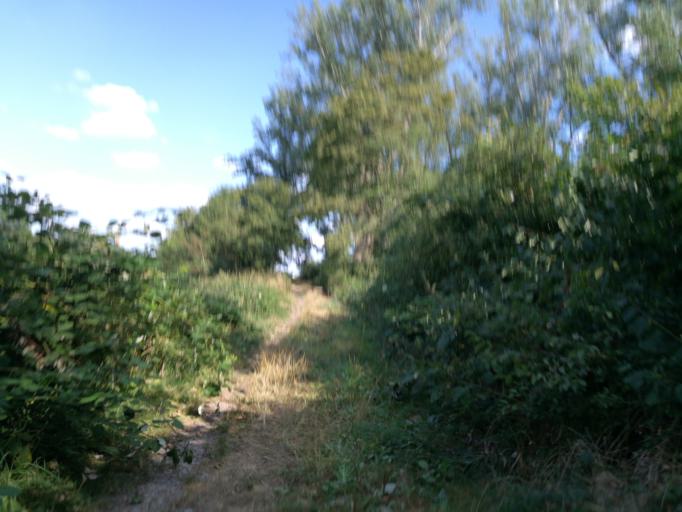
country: DE
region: Bavaria
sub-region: Regierungsbezirk Mittelfranken
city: Seukendorf
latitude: 49.4849
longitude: 10.9128
